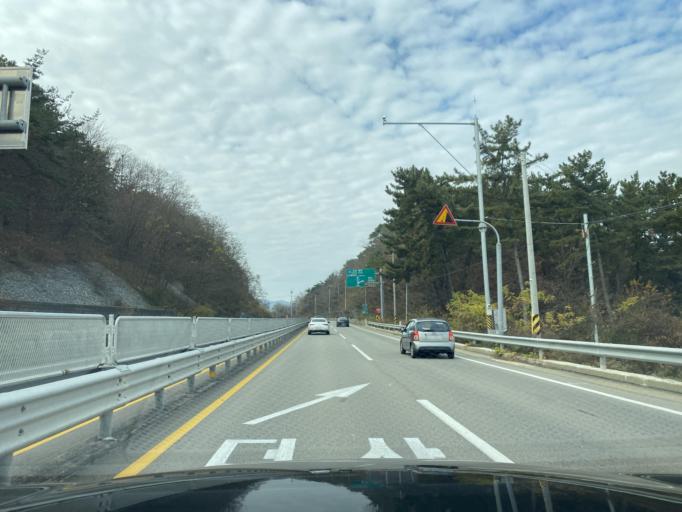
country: KR
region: Chungcheongnam-do
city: Hongsung
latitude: 36.6876
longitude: 126.6673
